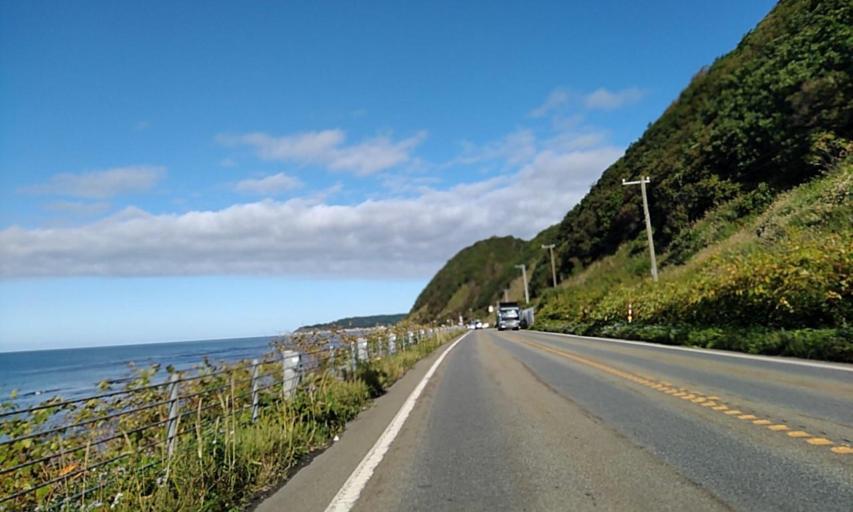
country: JP
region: Hokkaido
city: Shizunai-furukawacho
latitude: 42.2572
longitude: 142.5306
